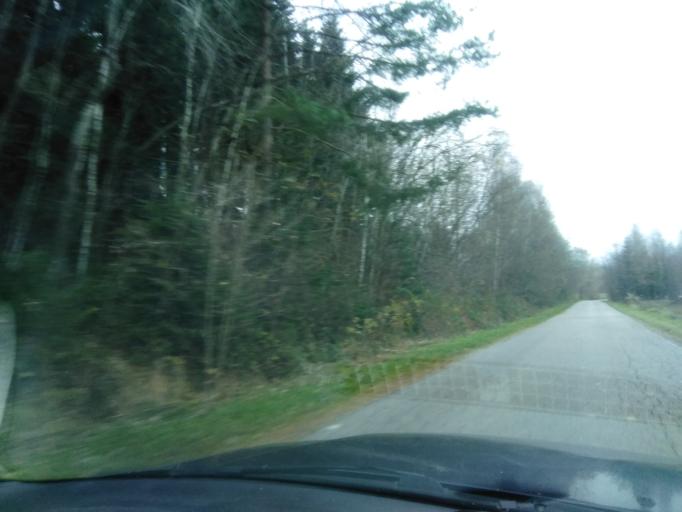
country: PL
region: Subcarpathian Voivodeship
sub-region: Powiat strzyzowski
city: Wysoka Strzyzowska
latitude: 49.8307
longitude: 21.7744
